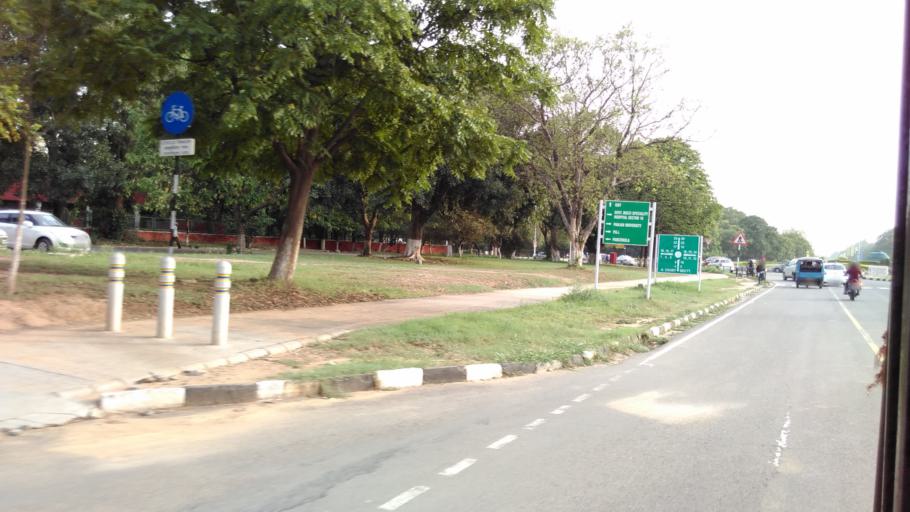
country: IN
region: Chandigarh
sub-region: Chandigarh
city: Chandigarh
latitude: 30.7473
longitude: 76.7869
